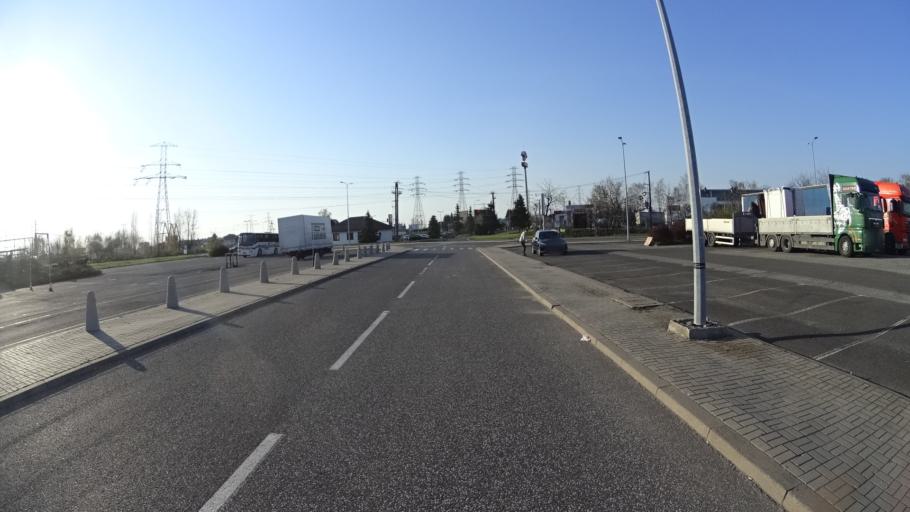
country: PL
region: Masovian Voivodeship
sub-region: Warszawa
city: Ursus
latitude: 52.2150
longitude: 20.8814
